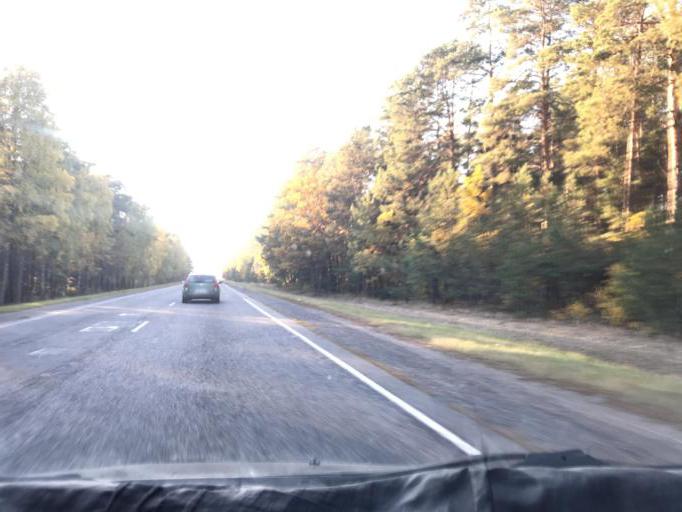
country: BY
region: Gomel
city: Zhytkavichy
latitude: 52.2727
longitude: 28.0356
